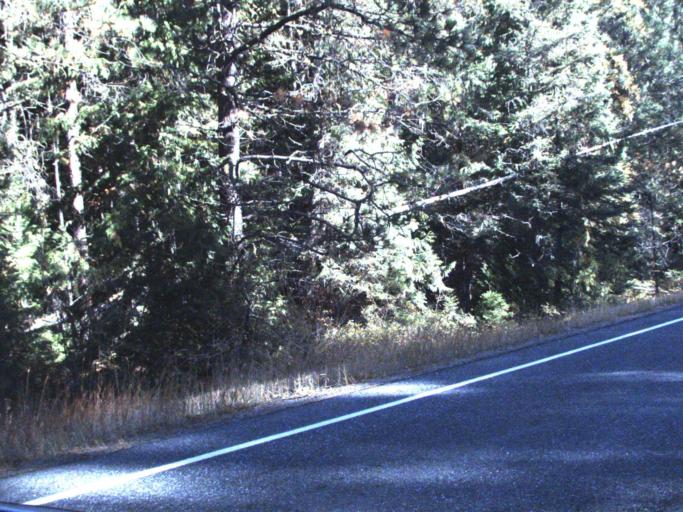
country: US
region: Washington
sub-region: Stevens County
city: Kettle Falls
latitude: 48.5960
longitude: -118.3407
